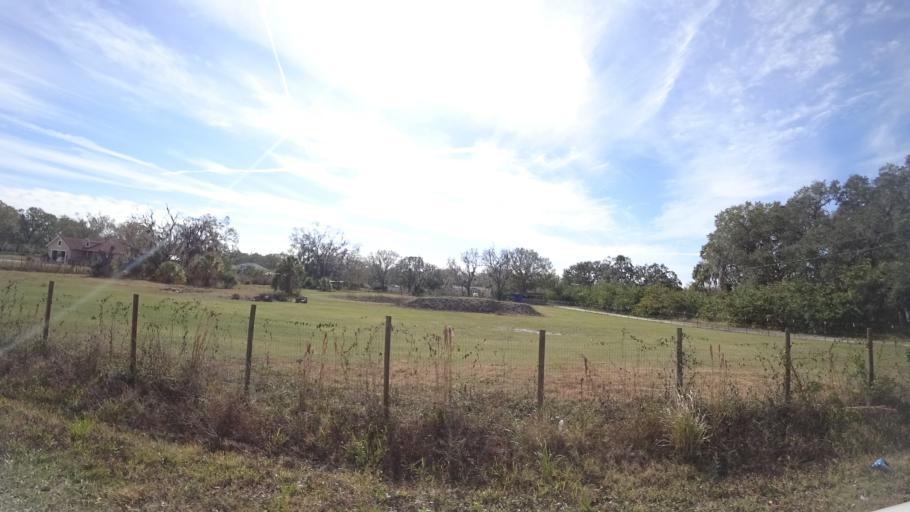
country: US
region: Florida
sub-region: Manatee County
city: Ellenton
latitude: 27.5762
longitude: -82.4374
